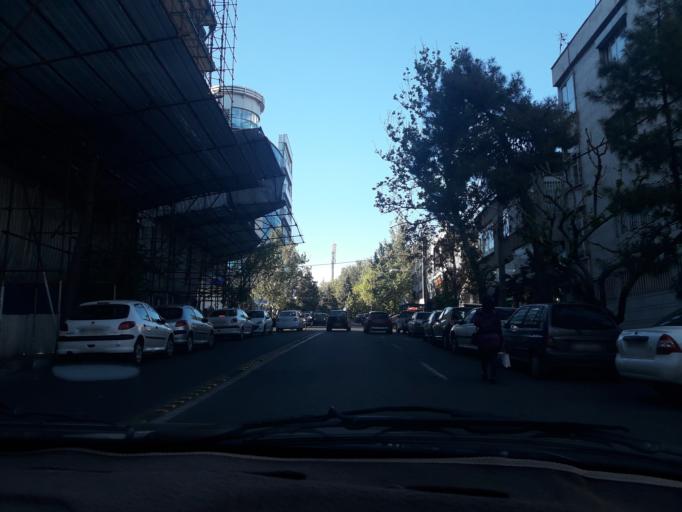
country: IR
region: Tehran
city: Tehran
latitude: 35.7219
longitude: 51.4025
